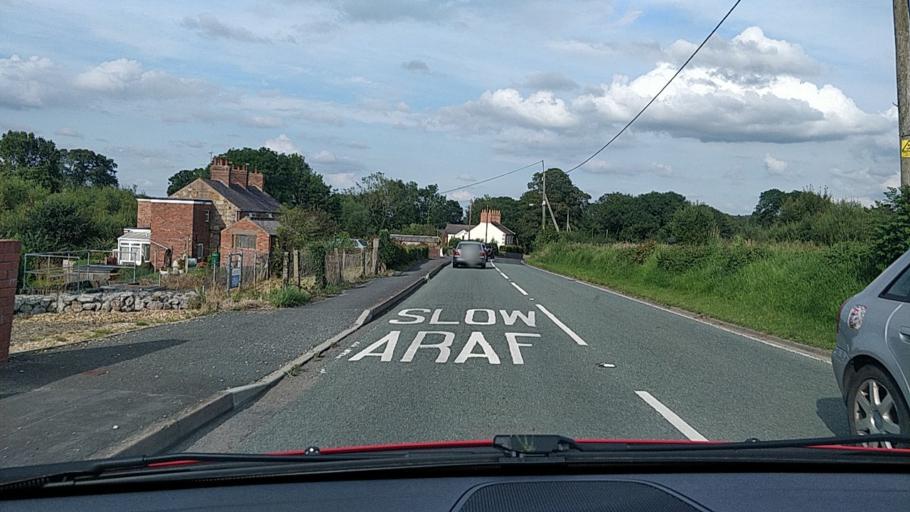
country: GB
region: Wales
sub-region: County of Flintshire
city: Leeswood
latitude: 53.1131
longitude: -3.1143
